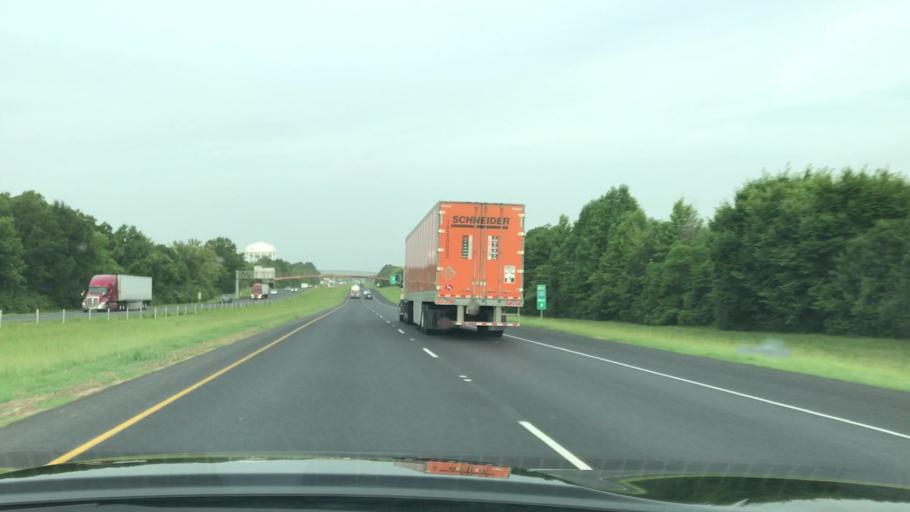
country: US
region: Louisiana
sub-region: Caddo Parish
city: Greenwood
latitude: 32.4468
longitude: -93.9062
